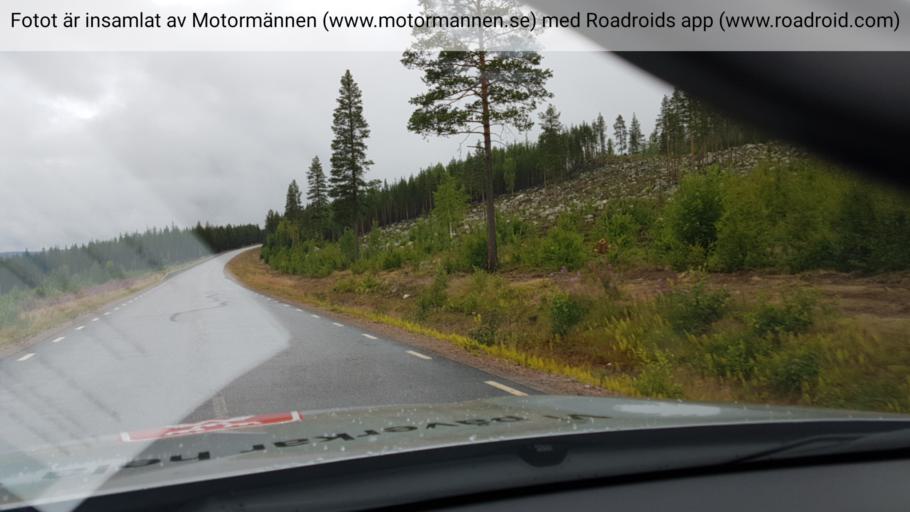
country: SE
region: Norrbotten
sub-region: Gallivare Kommun
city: Gaellivare
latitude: 66.6708
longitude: 20.3693
